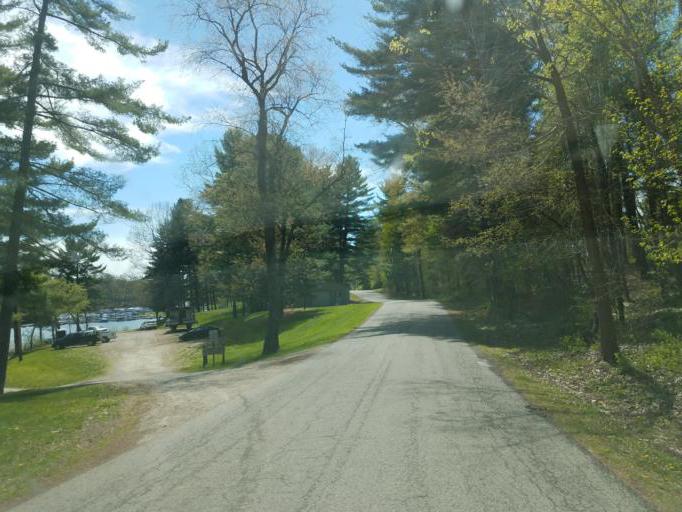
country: US
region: Ohio
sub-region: Richland County
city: Lincoln Heights
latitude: 40.7684
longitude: -82.3726
